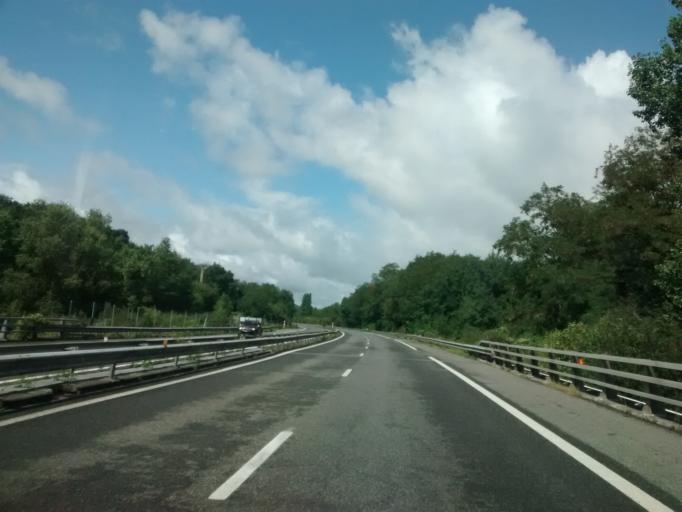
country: FR
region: Aquitaine
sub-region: Departement des Pyrenees-Atlantiques
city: Puyoo
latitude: 43.5112
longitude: -0.8866
